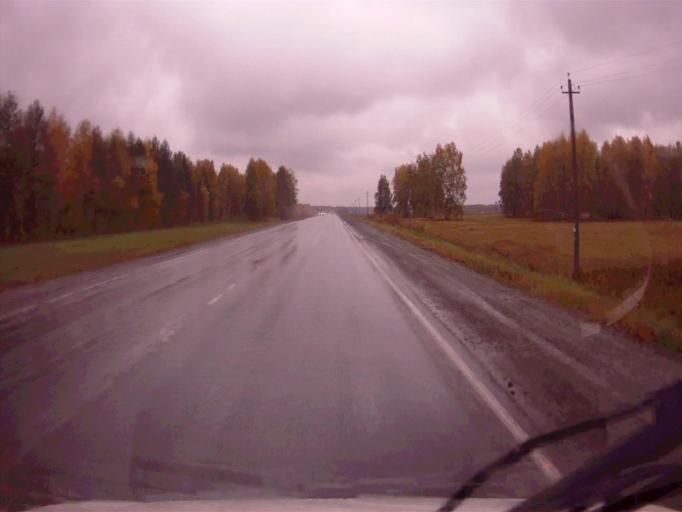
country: RU
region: Chelyabinsk
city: Argayash
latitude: 55.4016
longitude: 61.0706
